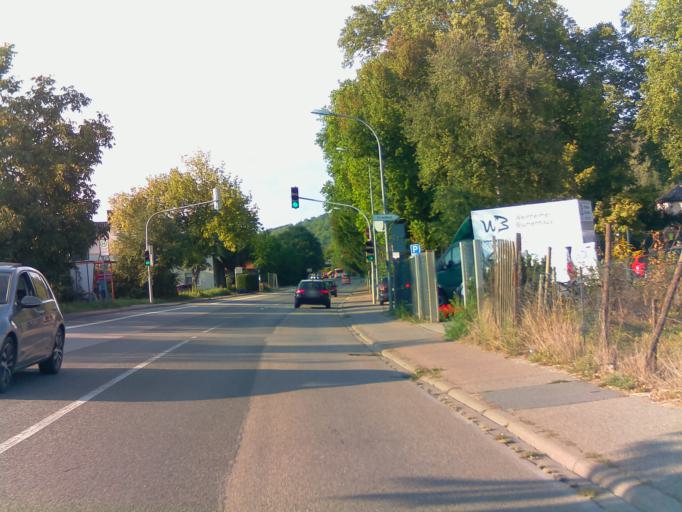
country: DE
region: Baden-Wuerttemberg
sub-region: Karlsruhe Region
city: Weinheim
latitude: 49.5667
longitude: 8.6638
